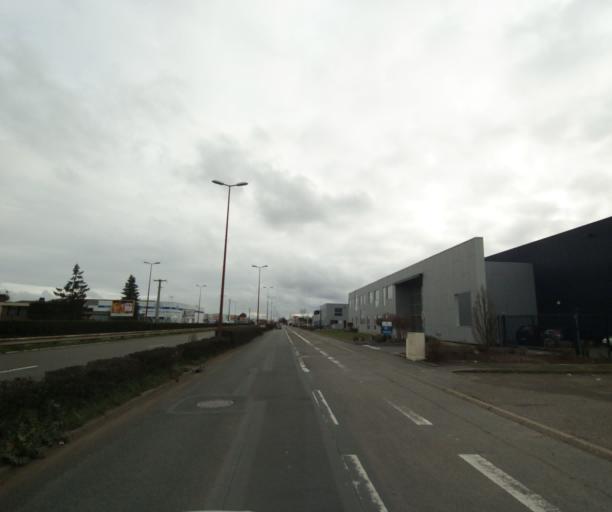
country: FR
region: Pays de la Loire
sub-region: Departement de la Sarthe
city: Allonnes
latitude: 47.9677
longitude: 0.1754
